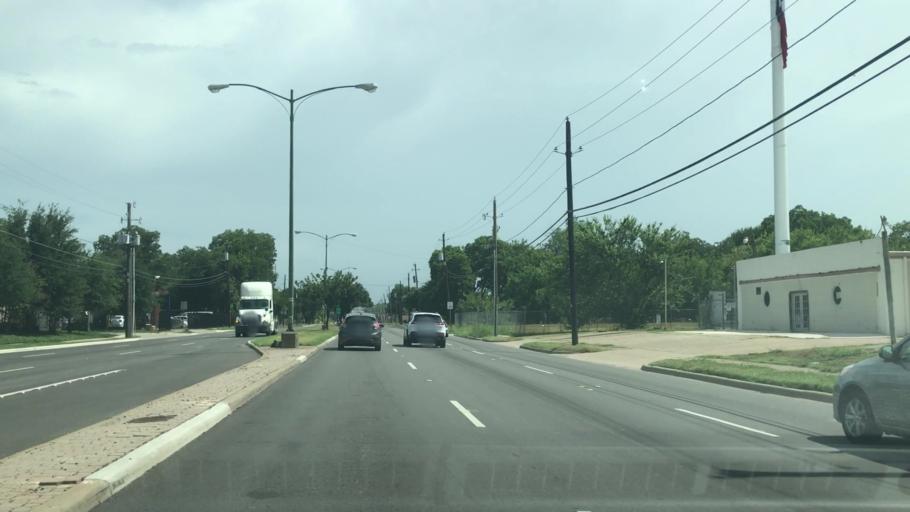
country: US
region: Texas
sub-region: Dallas County
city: Cockrell Hill
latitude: 32.7897
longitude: -96.8738
